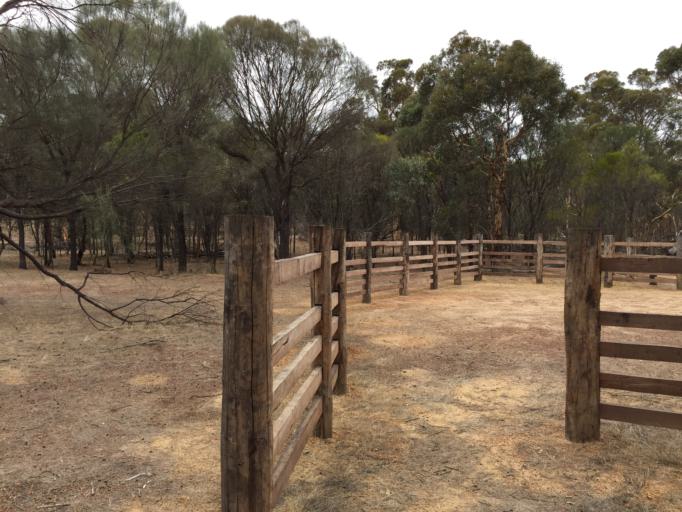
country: AU
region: Western Australia
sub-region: Narrogin
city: Narrogin
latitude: -32.8209
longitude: 116.8889
